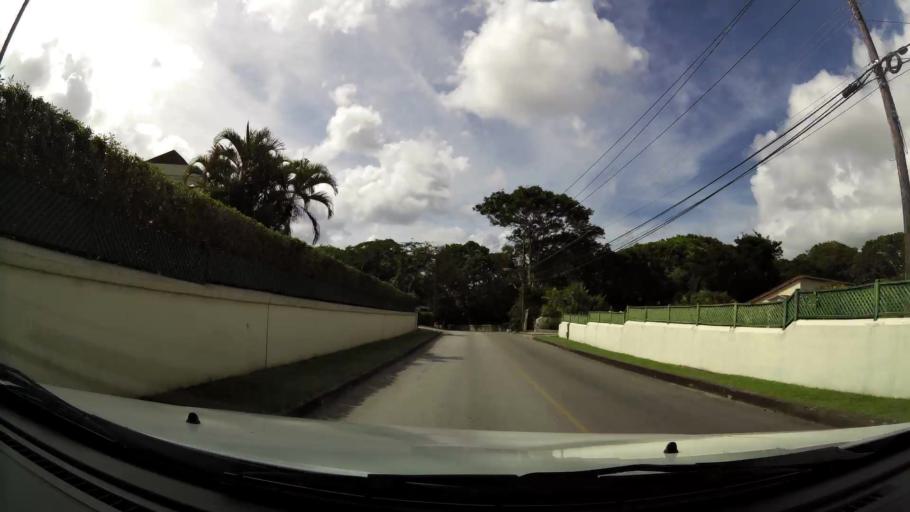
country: BB
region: Saint Michael
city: Bridgetown
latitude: 13.1002
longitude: -59.5953
